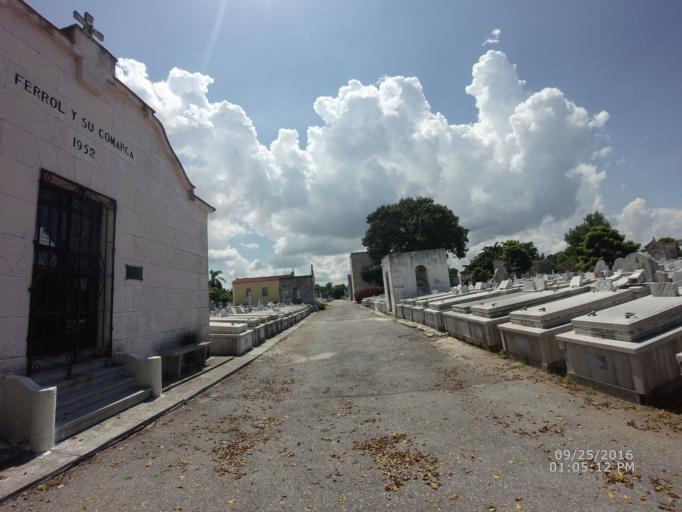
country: CU
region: La Habana
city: Havana
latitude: 23.1222
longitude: -82.4005
